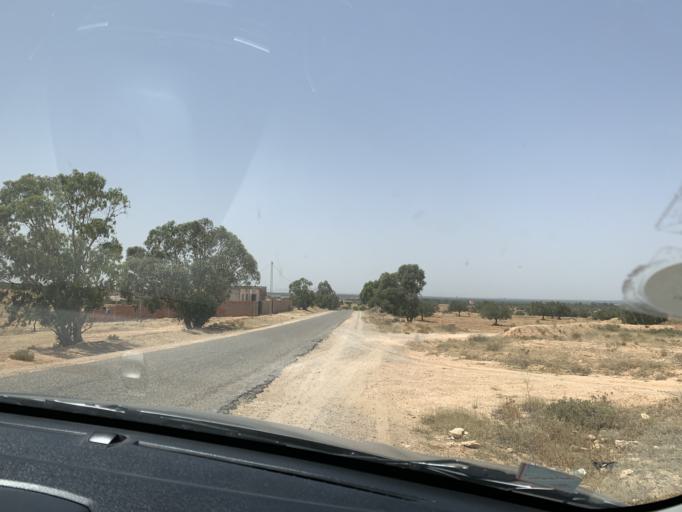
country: TN
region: Al Mahdiyah
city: Shurban
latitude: 35.1615
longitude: 10.2482
